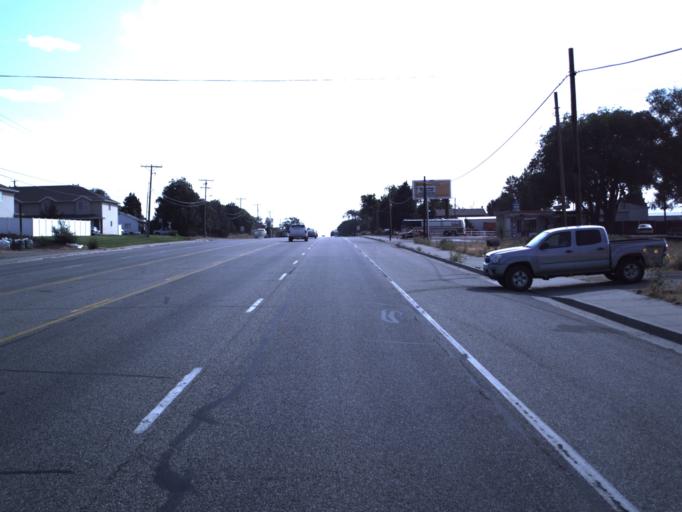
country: US
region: Utah
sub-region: Box Elder County
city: Perry
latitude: 41.4728
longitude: -112.0271
